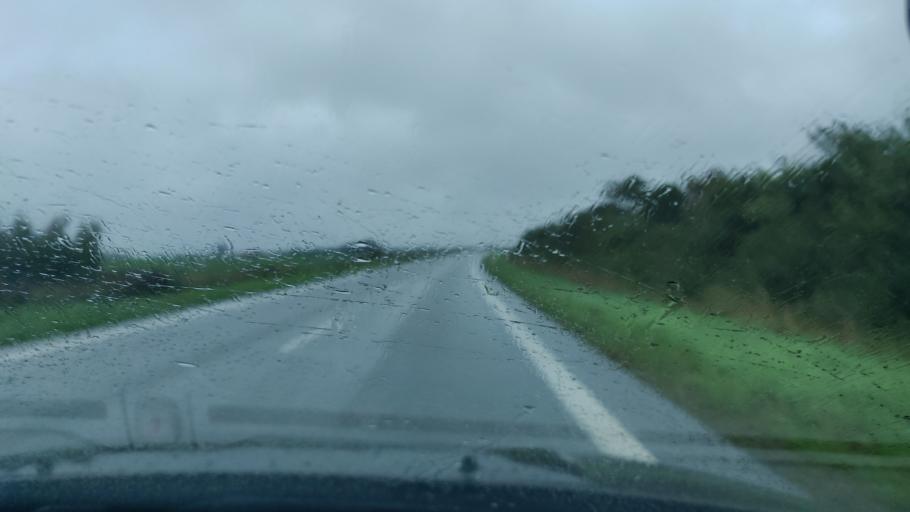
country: DK
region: North Denmark
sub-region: Thisted Kommune
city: Hurup
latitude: 56.8225
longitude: 8.4952
